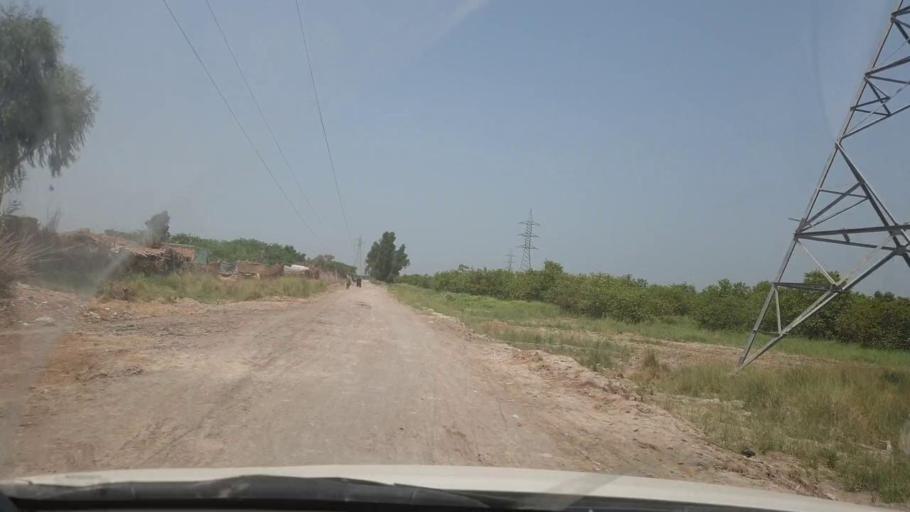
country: PK
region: Sindh
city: Lakhi
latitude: 27.8603
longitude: 68.6994
